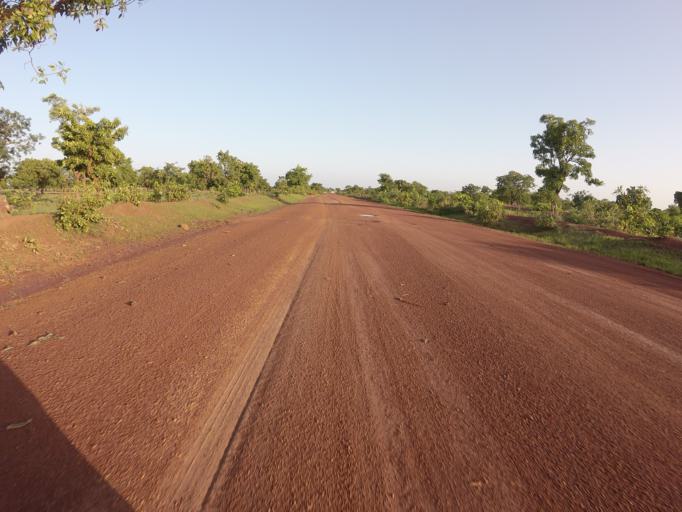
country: TG
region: Savanes
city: Sansanne-Mango
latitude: 10.2748
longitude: -0.0827
